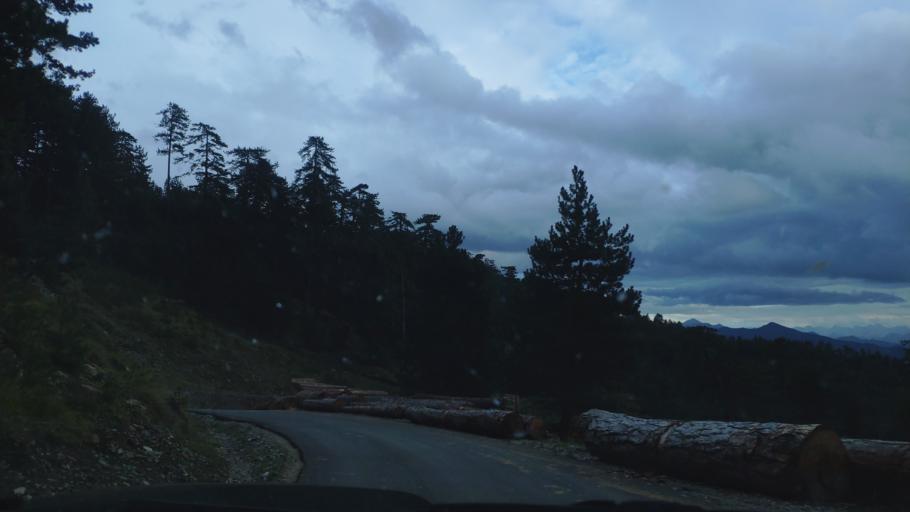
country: AL
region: Korce
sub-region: Rrethi i Kolonjes
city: Erseke
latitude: 40.2898
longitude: 20.8651
